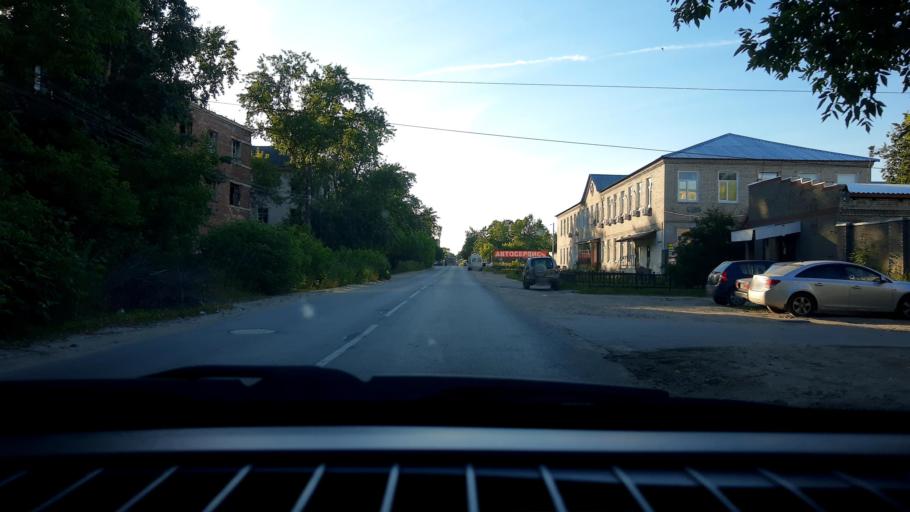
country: RU
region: Nizjnij Novgorod
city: Dzerzhinsk
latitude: 56.2403
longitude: 43.4887
